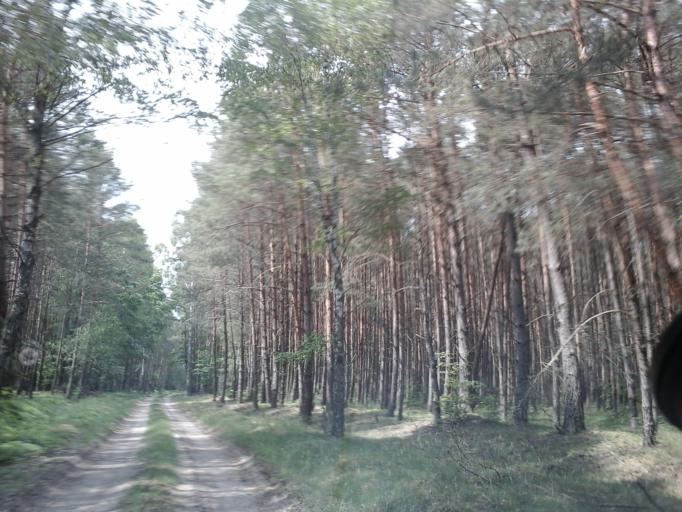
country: PL
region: West Pomeranian Voivodeship
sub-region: Powiat choszczenski
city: Drawno
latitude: 53.1115
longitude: 15.8739
